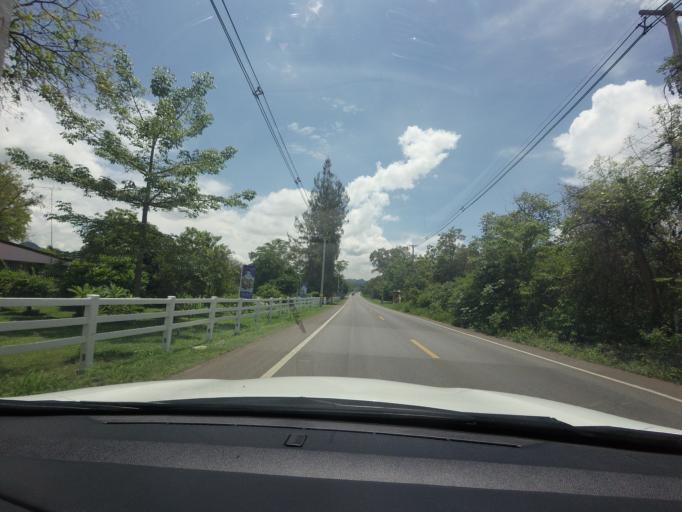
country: TH
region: Sara Buri
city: Muak Lek
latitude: 14.5935
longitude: 101.2198
